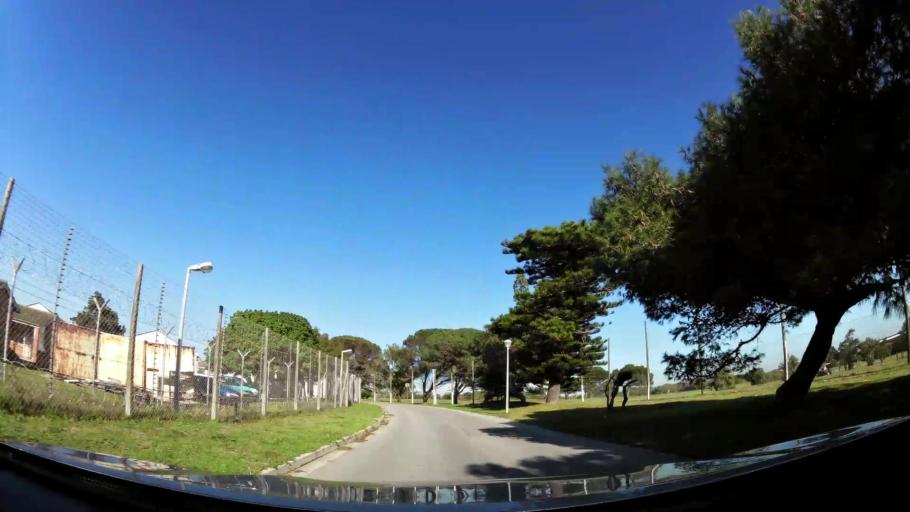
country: ZA
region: Eastern Cape
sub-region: Nelson Mandela Bay Metropolitan Municipality
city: Port Elizabeth
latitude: -33.9835
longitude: 25.6262
